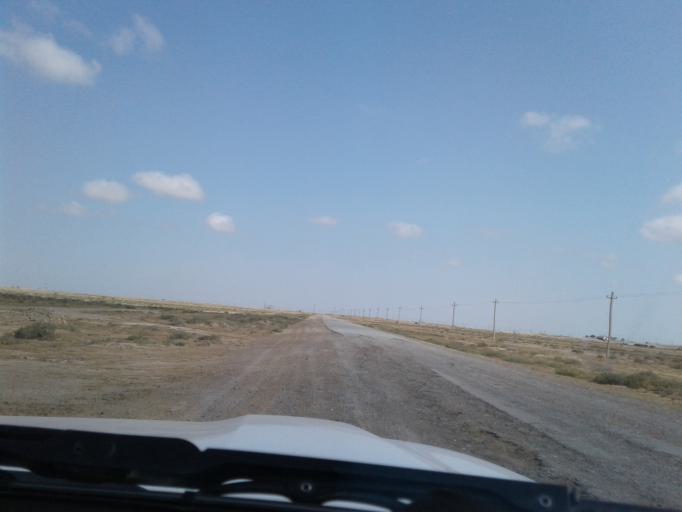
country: IR
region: Golestan
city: Gomishan
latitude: 37.7068
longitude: 53.9402
